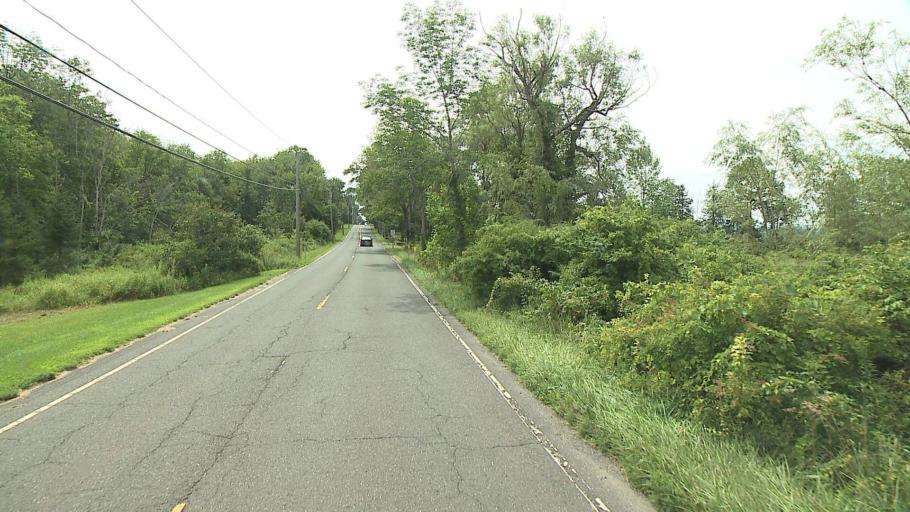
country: US
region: Connecticut
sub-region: Litchfield County
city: New Milford
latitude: 41.5208
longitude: -73.3633
